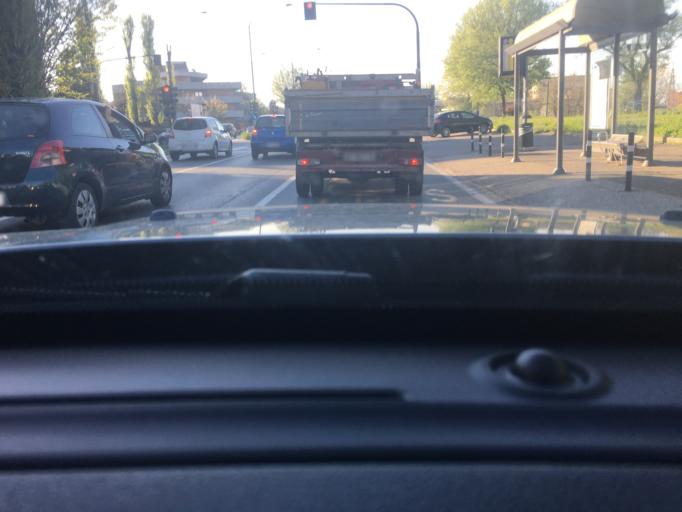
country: IT
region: Piedmont
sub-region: Provincia di Torino
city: Turin
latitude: 45.0967
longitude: 7.7139
